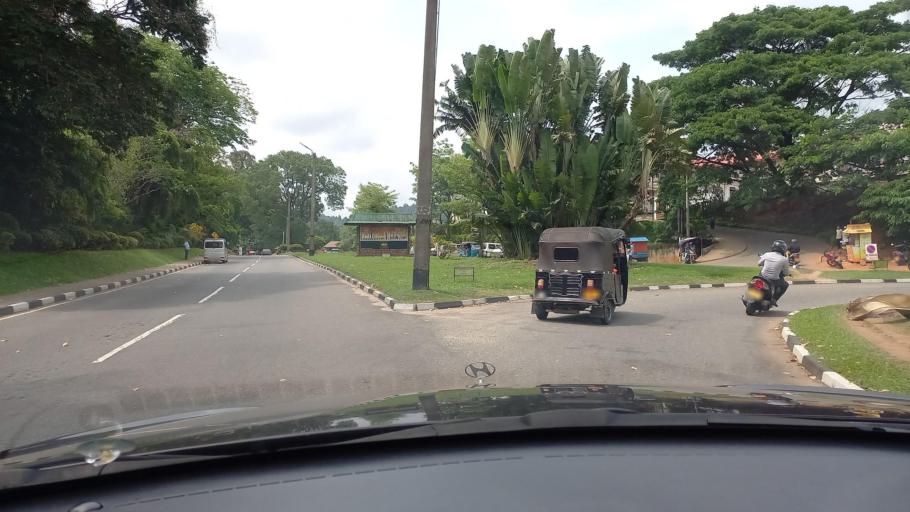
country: LK
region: Central
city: Kandy
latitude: 7.2662
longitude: 80.5961
